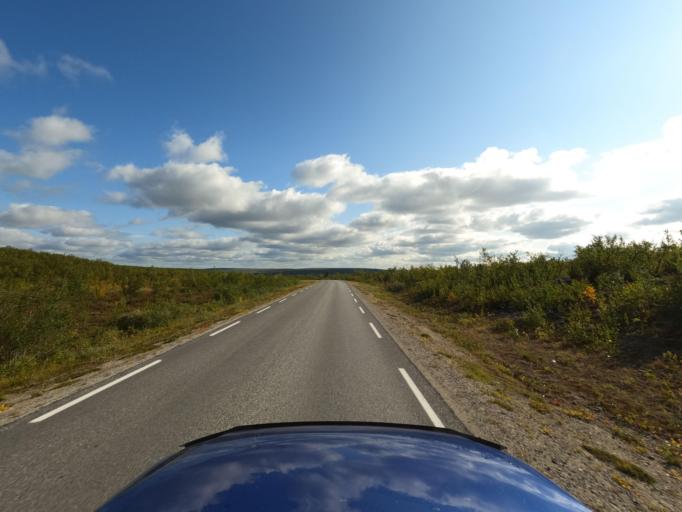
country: NO
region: Finnmark Fylke
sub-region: Porsanger
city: Lakselv
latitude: 69.3937
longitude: 24.5756
